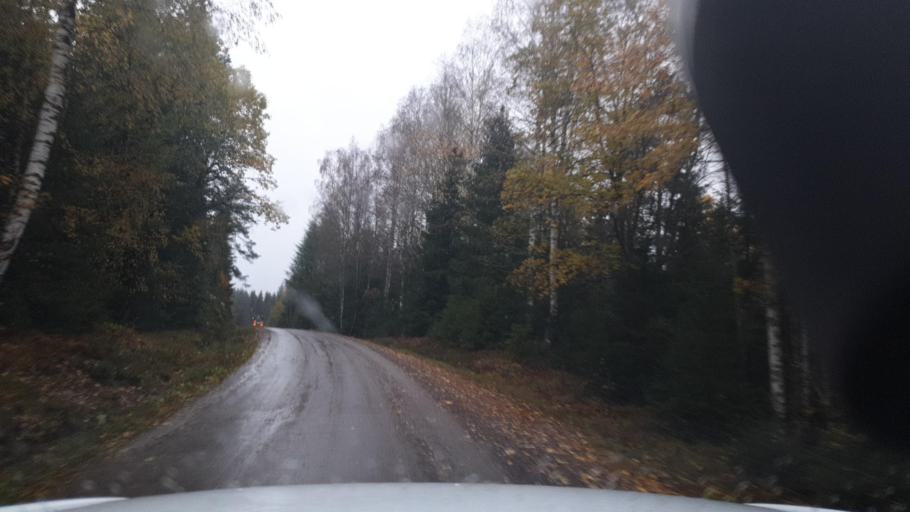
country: SE
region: Vaermland
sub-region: Eda Kommun
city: Amotfors
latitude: 59.8054
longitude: 12.4440
